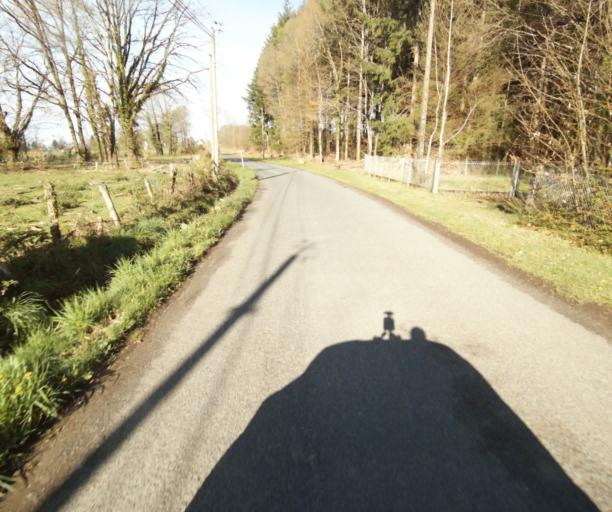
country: FR
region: Limousin
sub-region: Departement de la Correze
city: Laguenne
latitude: 45.2679
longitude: 1.8814
